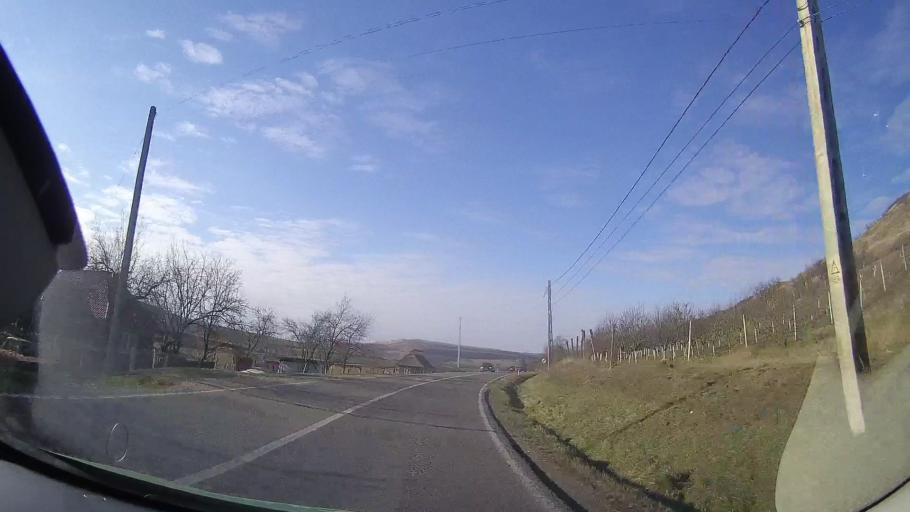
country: RO
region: Cluj
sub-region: Comuna Caianu
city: Vaida-Camaras
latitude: 46.7980
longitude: 23.9496
